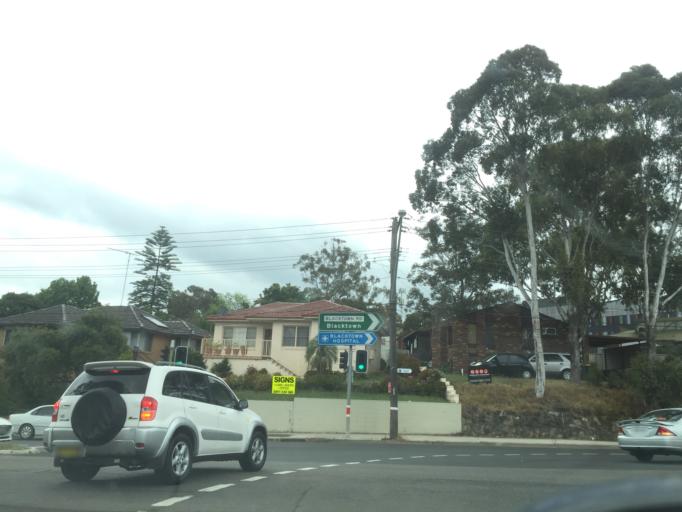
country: AU
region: New South Wales
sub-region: Blacktown
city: Blacktown
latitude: -33.7760
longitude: 150.9200
